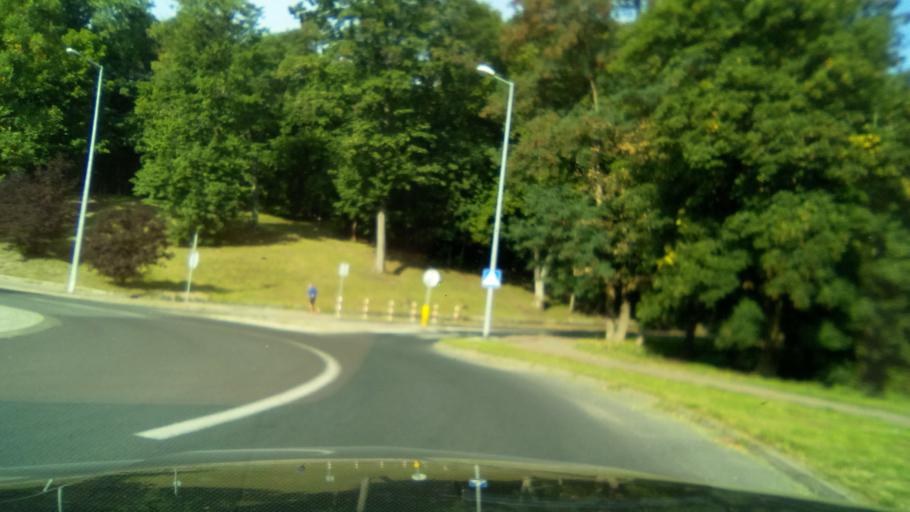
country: PL
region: Greater Poland Voivodeship
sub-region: Powiat pilski
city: Pila
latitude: 53.1449
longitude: 16.7269
